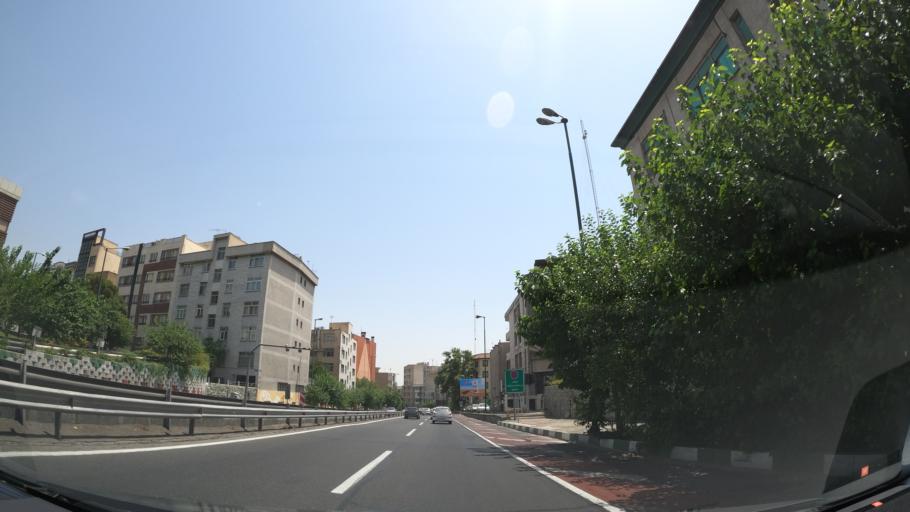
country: IR
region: Tehran
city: Tehran
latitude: 35.7236
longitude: 51.4250
